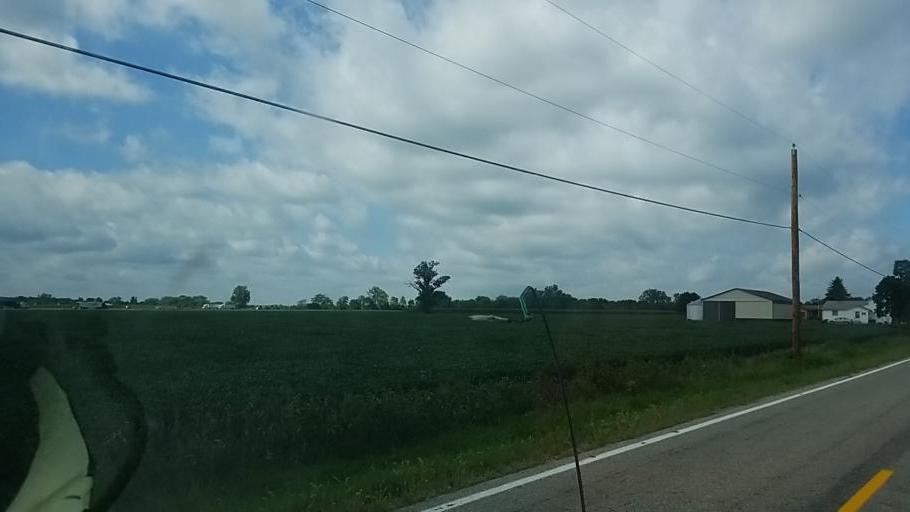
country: US
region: Ohio
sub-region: Madison County
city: Bethel
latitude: 39.7313
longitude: -83.3800
